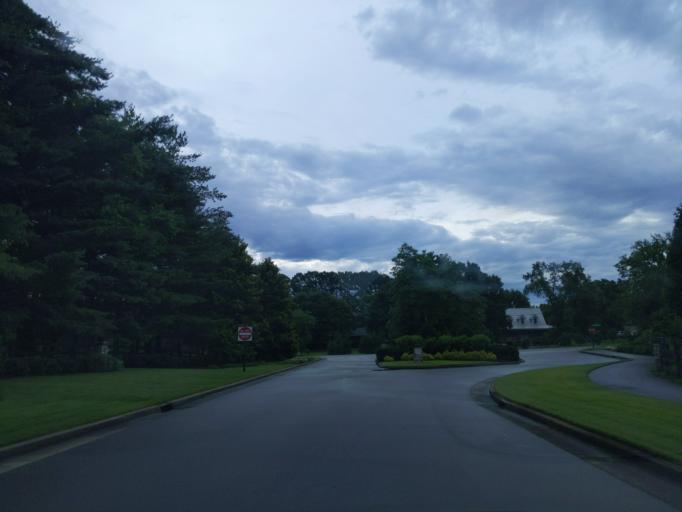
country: US
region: Tennessee
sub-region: Williamson County
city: Brentwood Estates
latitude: 36.0095
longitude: -86.7426
